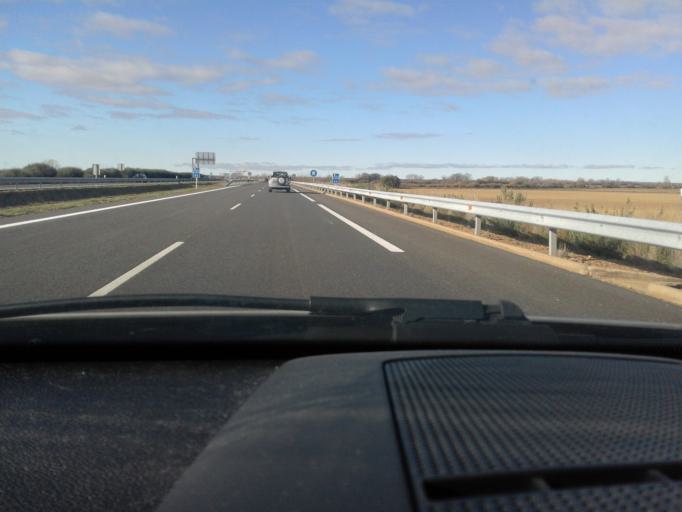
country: ES
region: Castille and Leon
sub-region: Provincia de Palencia
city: Calzada de los Molinos
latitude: 42.3500
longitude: -4.6329
